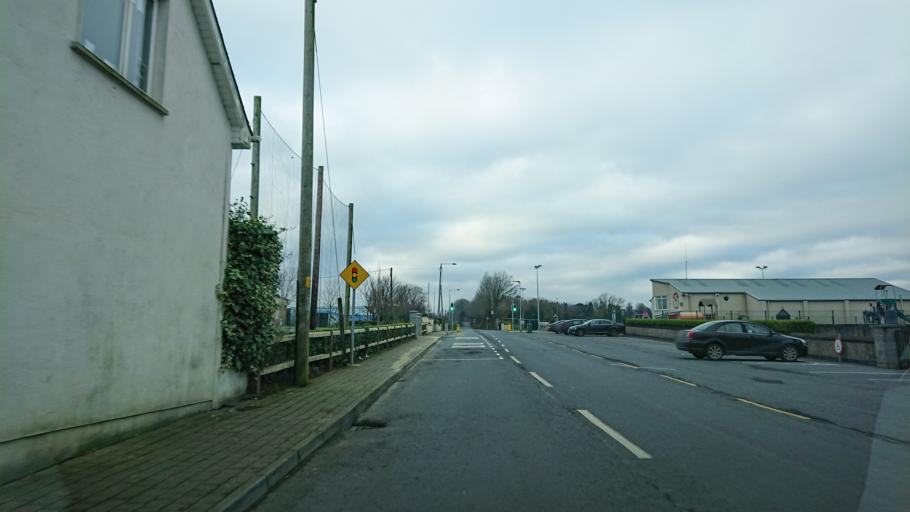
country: IE
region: Munster
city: Carrick-on-Suir
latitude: 52.3061
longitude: -7.4987
